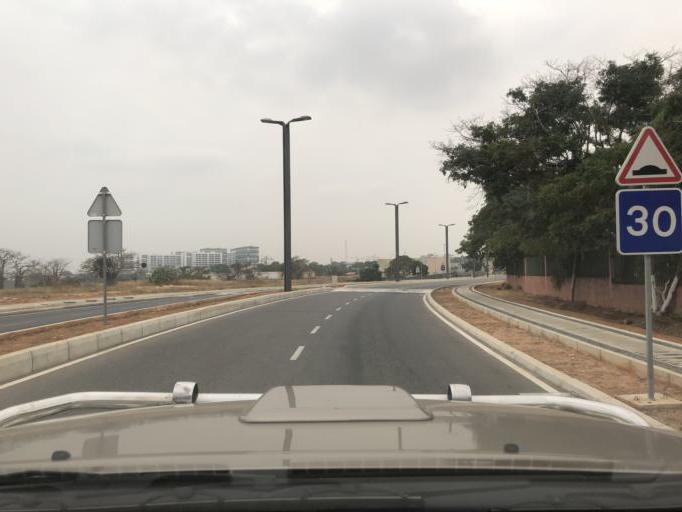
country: AO
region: Luanda
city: Luanda
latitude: -8.8937
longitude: 13.1756
